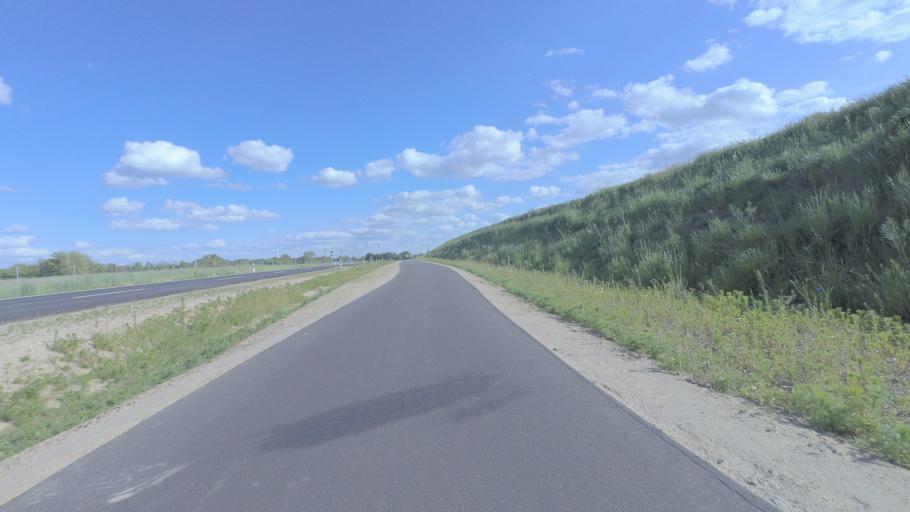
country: DE
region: Brandenburg
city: Stahnsdorf
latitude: 52.3786
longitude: 13.2352
